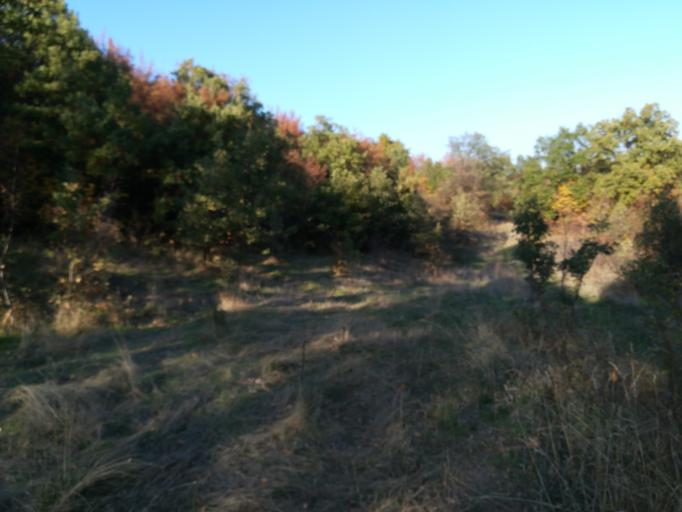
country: BG
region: Khaskovo
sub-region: Obshtina Mineralni Bani
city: Mineralni Bani
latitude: 41.9827
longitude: 25.2359
